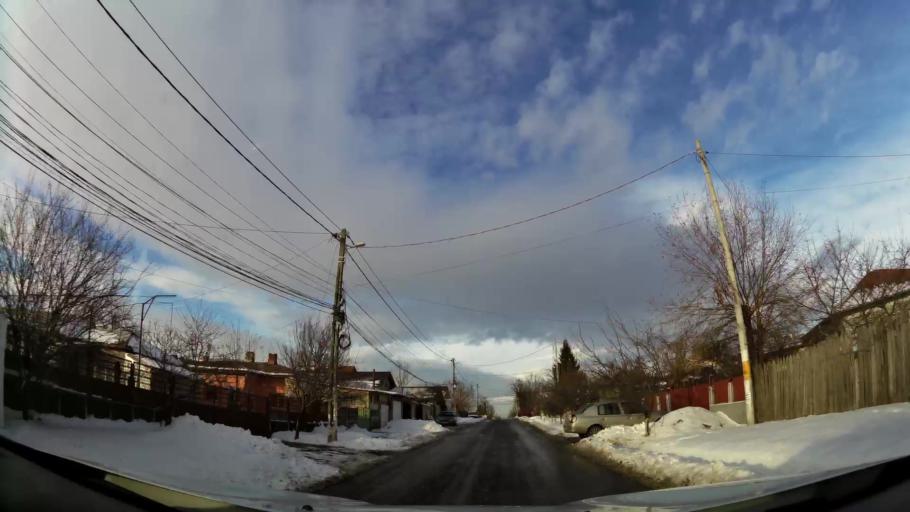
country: RO
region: Ilfov
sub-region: Comuna Jilava
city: Jilava
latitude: 44.3356
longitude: 26.0827
